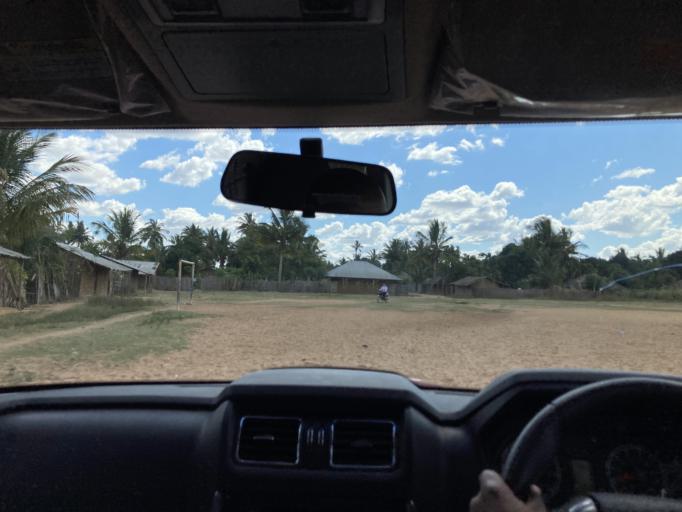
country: MZ
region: Cabo Delgado
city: Montepuez
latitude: -13.1452
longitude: 38.9987
